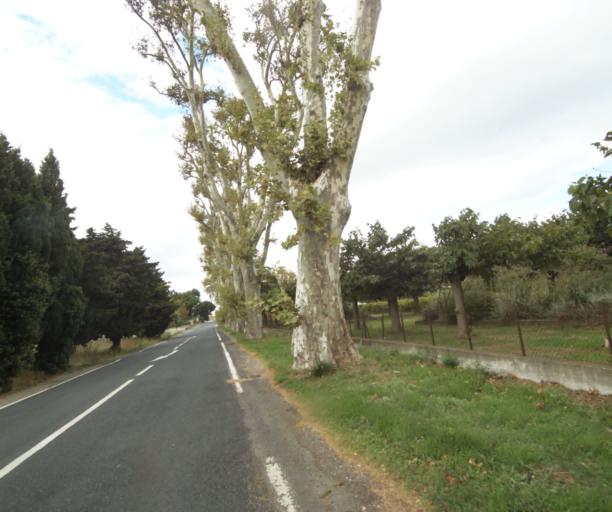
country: FR
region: Languedoc-Roussillon
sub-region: Departement des Pyrenees-Orientales
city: Elne
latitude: 42.5932
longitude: 2.9779
